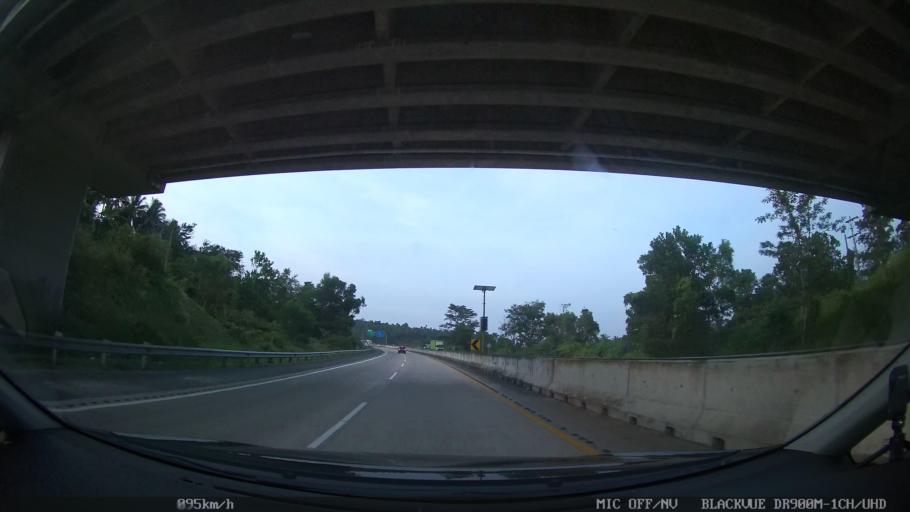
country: ID
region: Lampung
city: Penengahan
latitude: -5.8207
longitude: 105.7355
